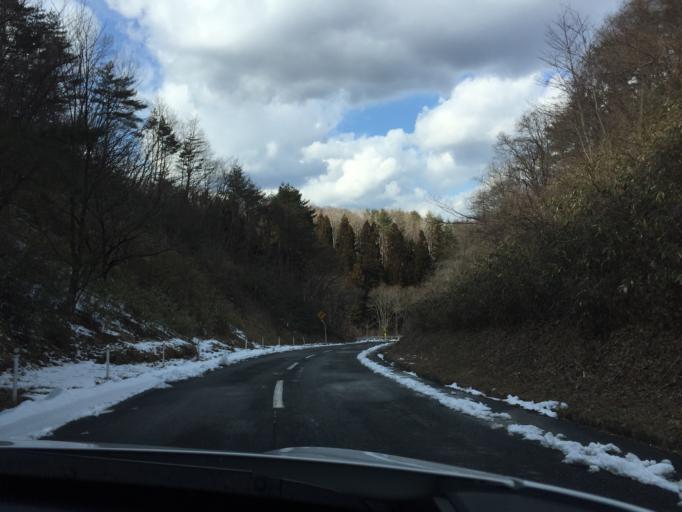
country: JP
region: Fukushima
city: Iwaki
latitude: 37.2015
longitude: 140.7119
